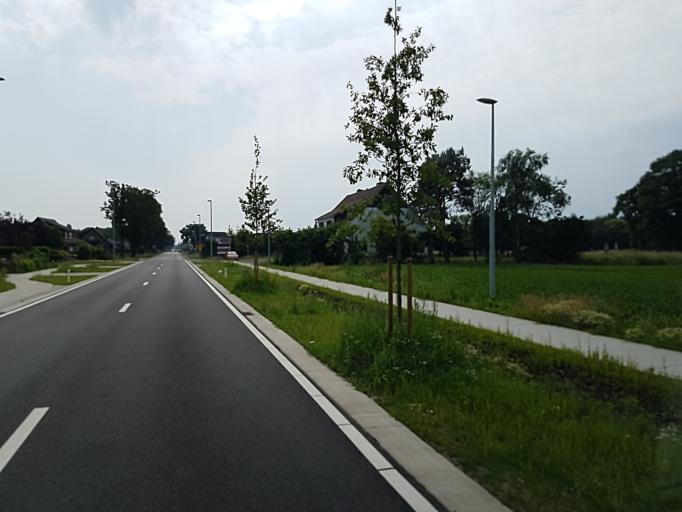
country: BE
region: Flanders
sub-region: Provincie Limburg
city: Leopoldsburg
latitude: 51.1351
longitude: 5.2373
